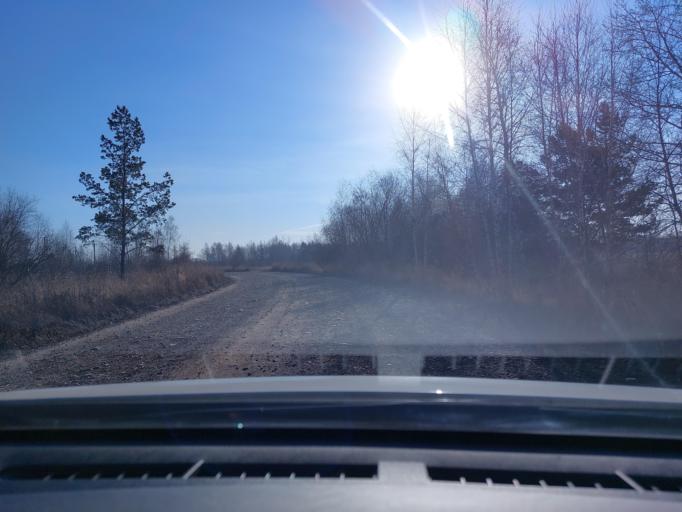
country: RU
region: Irkutsk
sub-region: Irkutskiy Rayon
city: Irkutsk
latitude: 52.3075
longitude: 104.2726
